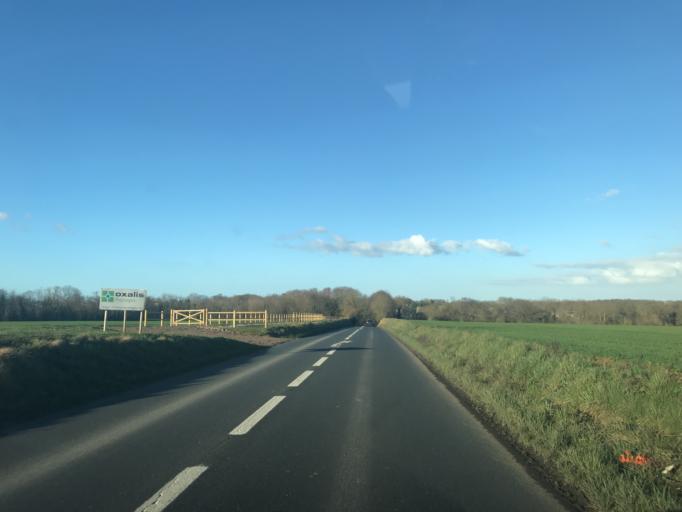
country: FR
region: Lower Normandy
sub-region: Departement du Calvados
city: Beuville
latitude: 49.2236
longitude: -0.3365
